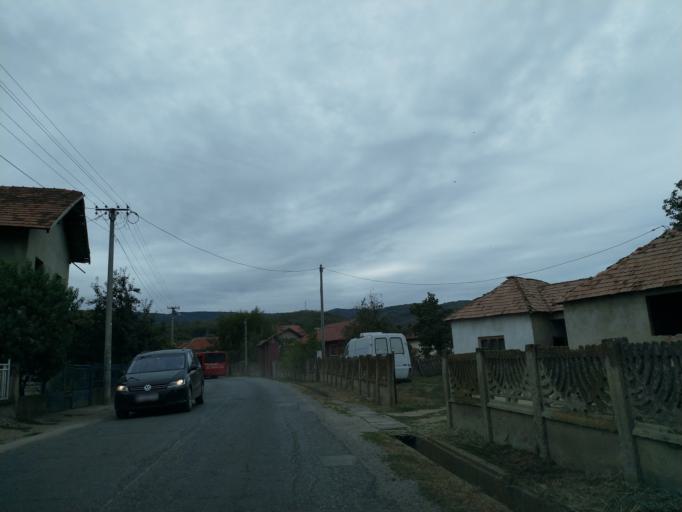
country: RS
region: Central Serbia
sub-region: Pomoravski Okrug
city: Paracin
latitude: 43.8355
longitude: 21.3255
